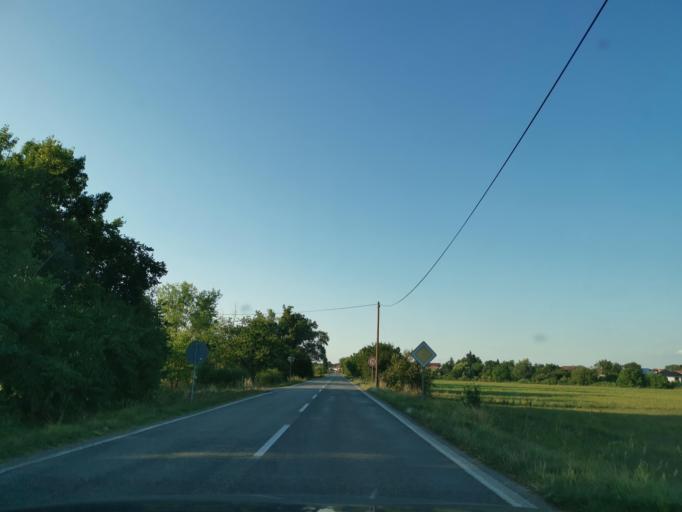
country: AT
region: Lower Austria
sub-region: Politischer Bezirk Mistelbach
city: Rabensburg
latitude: 48.5975
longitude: 16.9947
